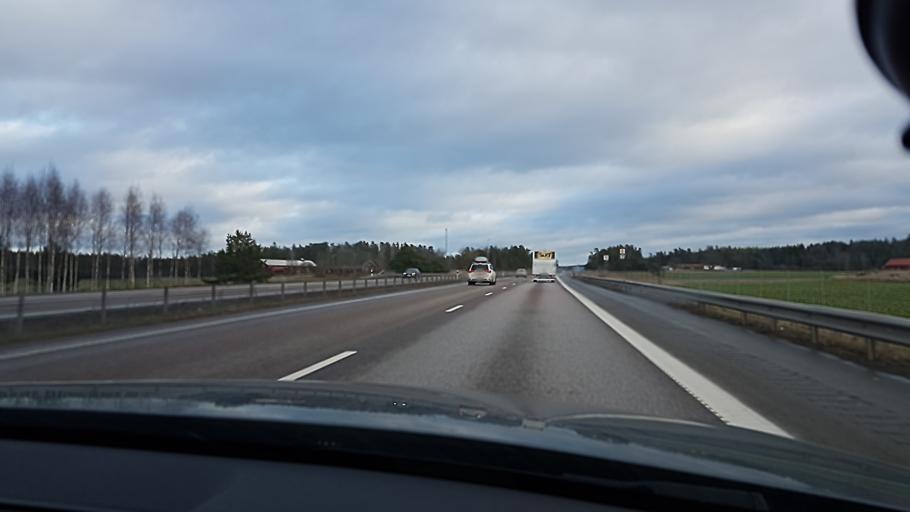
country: SE
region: OEstergoetland
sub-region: Linkopings Kommun
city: Linghem
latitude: 58.4793
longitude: 15.8595
